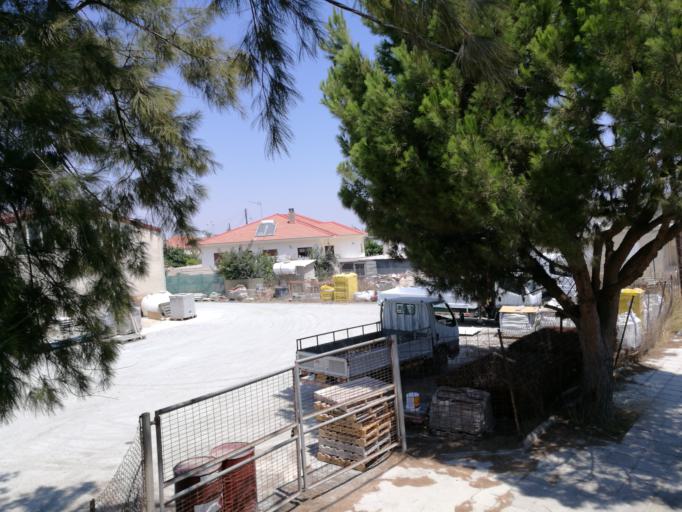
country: CY
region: Larnaka
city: Kiti
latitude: 34.8519
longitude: 33.5757
